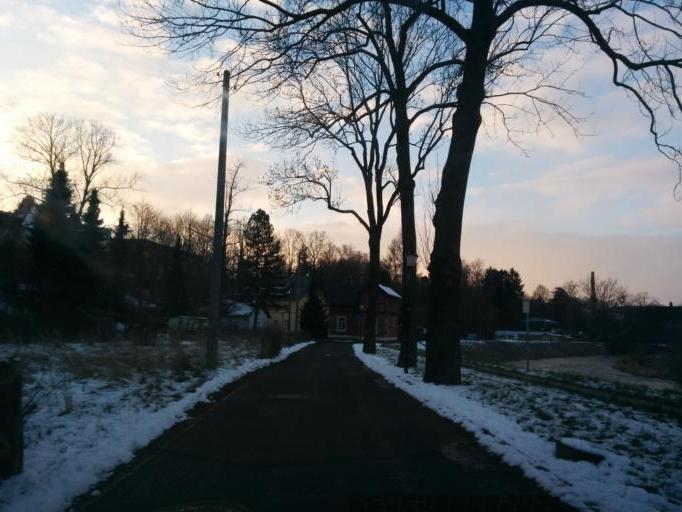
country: DE
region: Saxony
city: Floha
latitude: 50.8477
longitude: 13.0769
